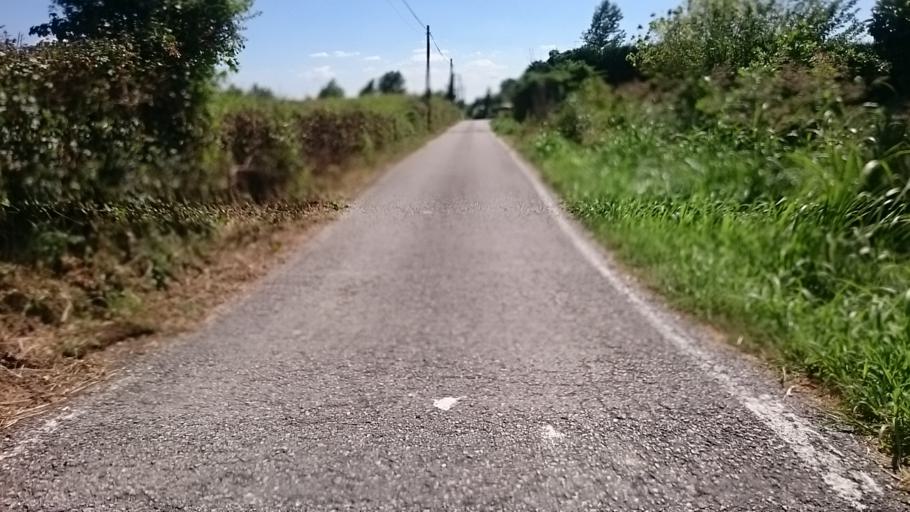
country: IT
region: Veneto
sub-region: Provincia di Venezia
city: Fiesso d'Artico
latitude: 45.4393
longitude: 12.0258
